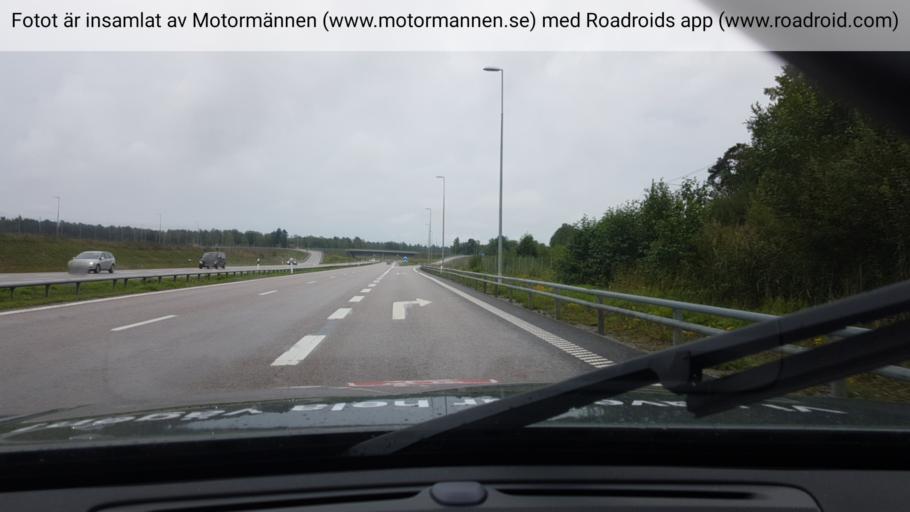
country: SE
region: Stockholm
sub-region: Nynashamns Kommun
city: Osmo
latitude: 58.9463
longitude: 17.9071
